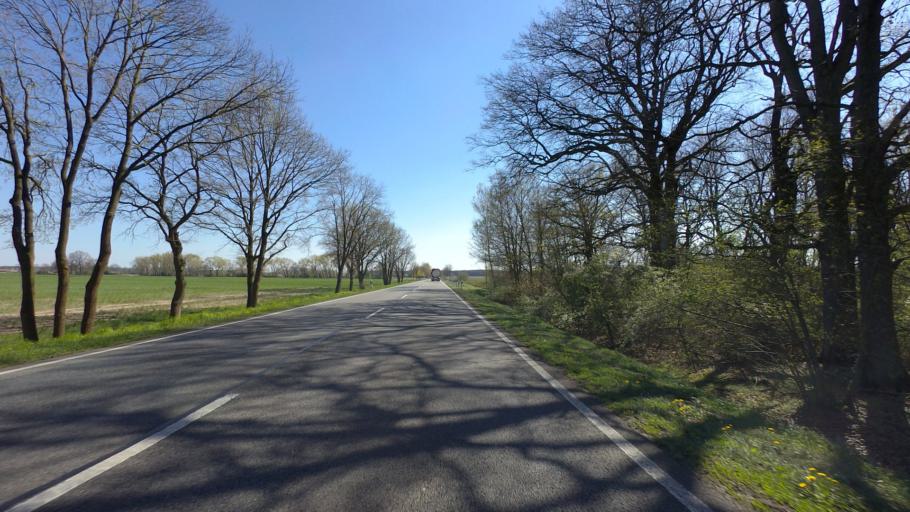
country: DE
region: Saxony-Anhalt
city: Pretzier
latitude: 52.7647
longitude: 11.2376
